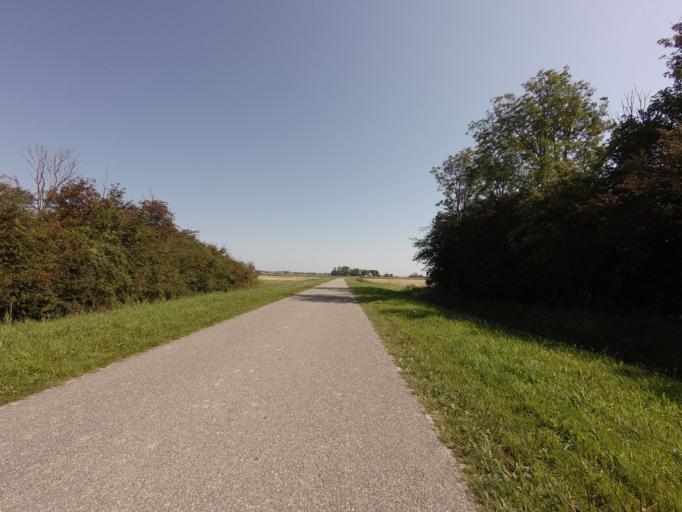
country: NL
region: Friesland
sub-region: Gemeente Dongeradeel
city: Ternaard
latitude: 53.3684
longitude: 5.9363
